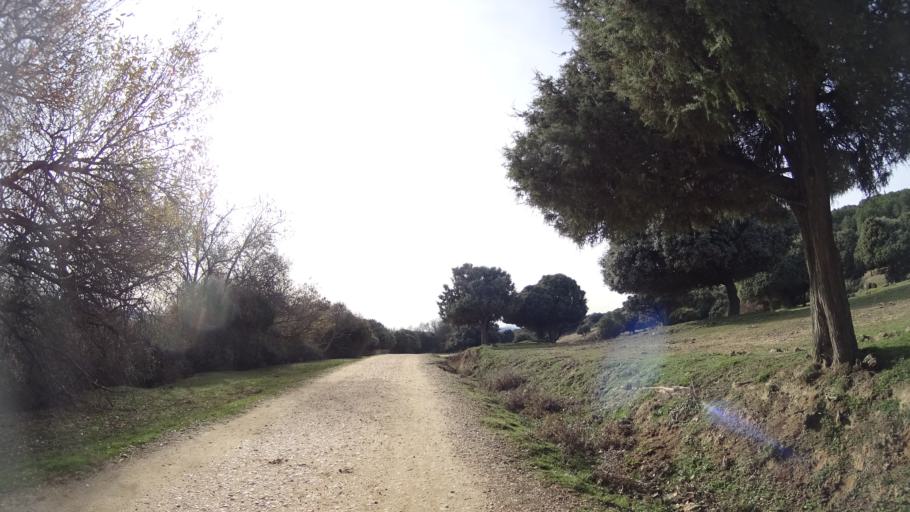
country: ES
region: Madrid
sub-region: Provincia de Madrid
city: Moralzarzal
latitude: 40.6670
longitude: -3.9889
